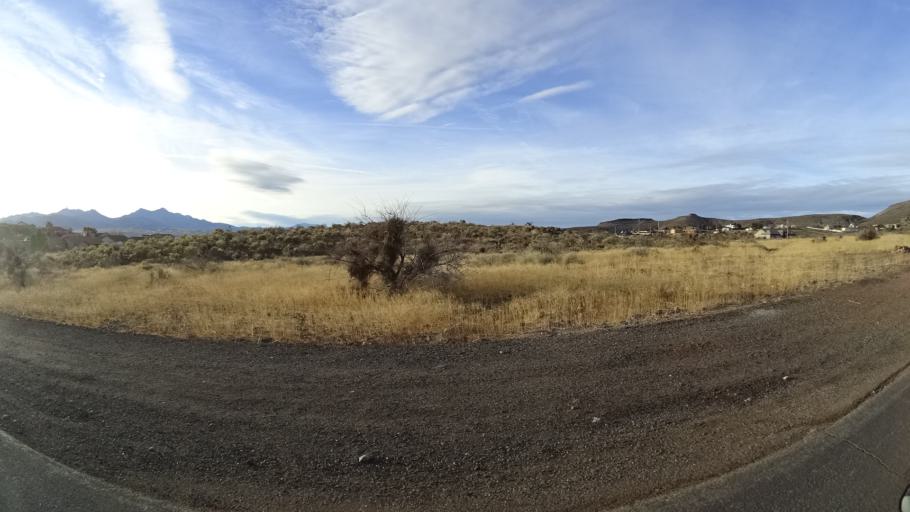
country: US
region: Arizona
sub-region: Mohave County
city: New Kingman-Butler
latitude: 35.2419
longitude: -114.0483
